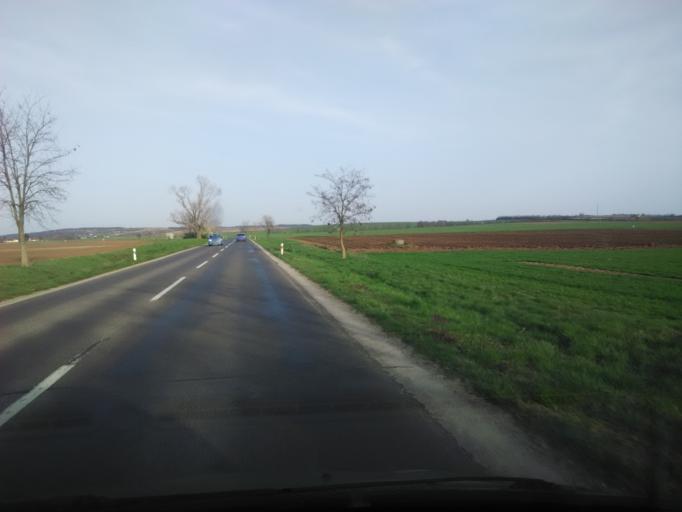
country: SK
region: Nitriansky
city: Surany
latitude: 48.0901
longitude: 18.2709
